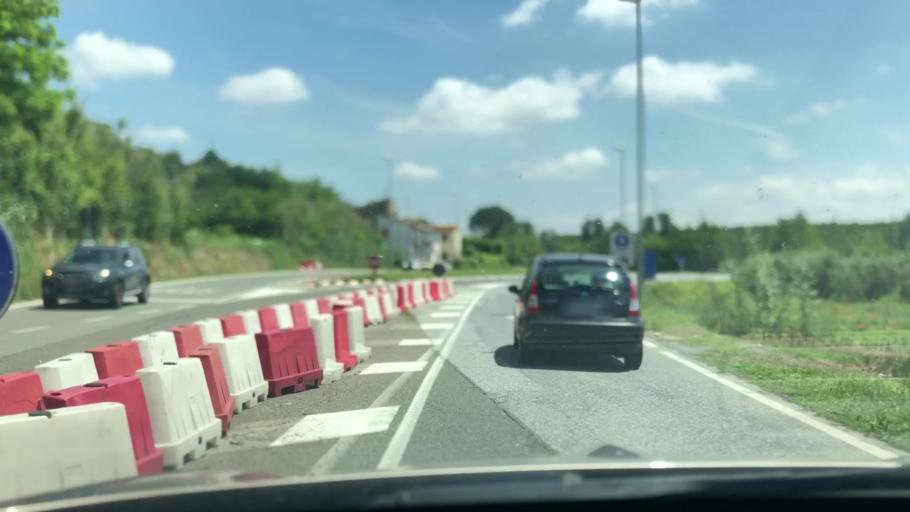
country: IT
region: Tuscany
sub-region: Province of Pisa
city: Forcoli
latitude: 43.6104
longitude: 10.6891
